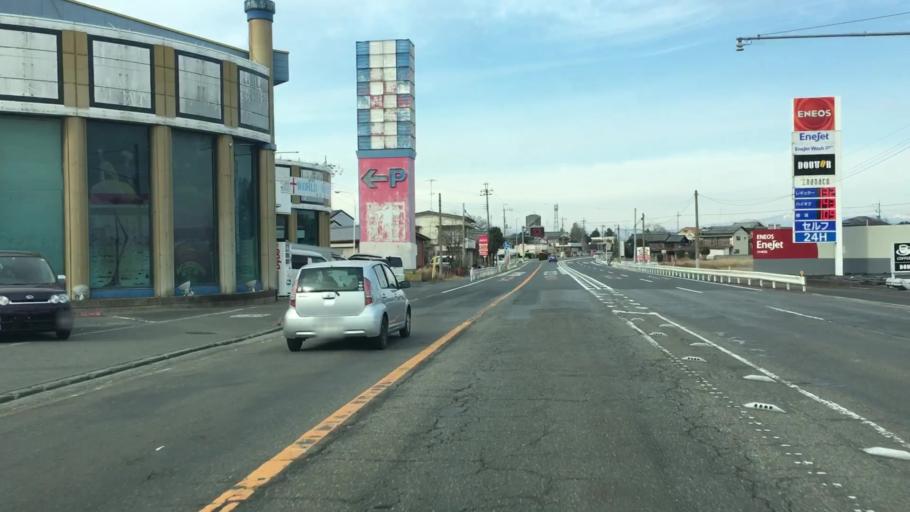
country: JP
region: Saitama
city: Menuma
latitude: 36.2453
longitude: 139.3803
